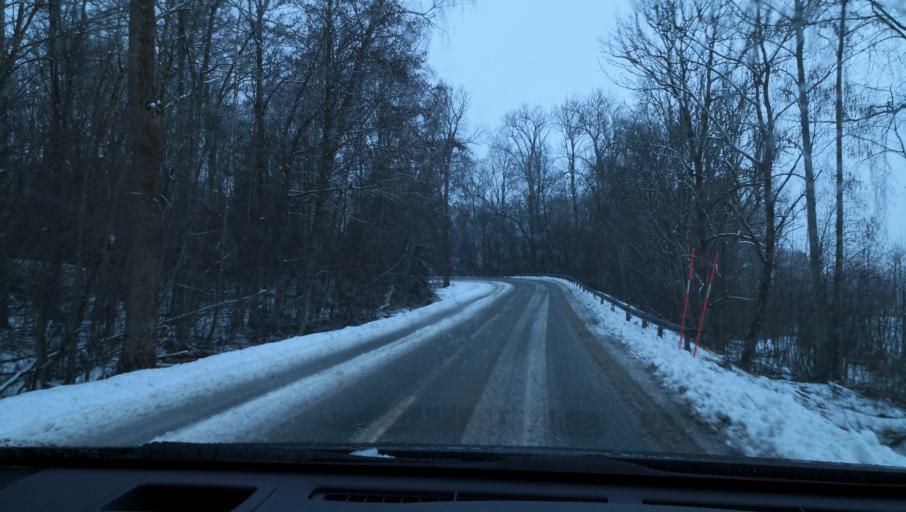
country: SE
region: Vaestmanland
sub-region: Kopings Kommun
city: Kolsva
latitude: 59.5963
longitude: 15.8286
